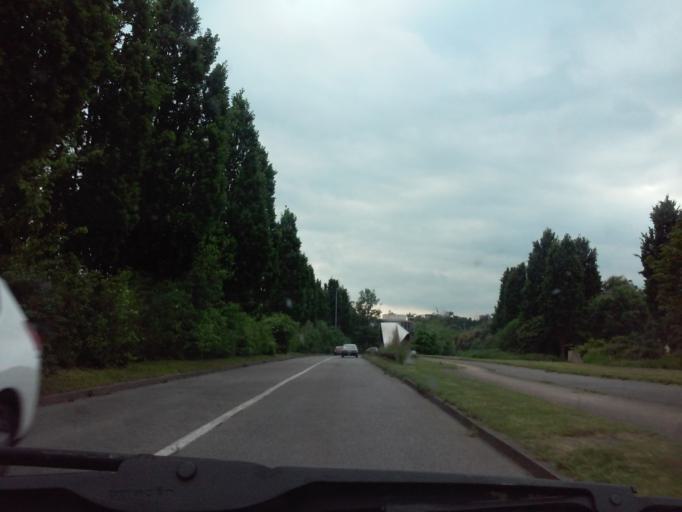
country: FR
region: Brittany
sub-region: Departement d'Ille-et-Vilaine
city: Chantepie
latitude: 48.0922
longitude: -1.6411
